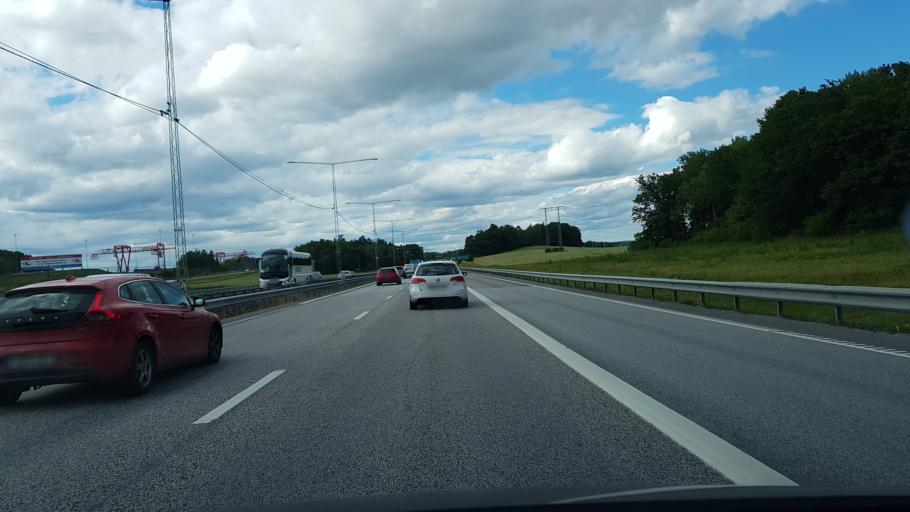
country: SE
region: Stockholm
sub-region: Sigtuna Kommun
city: Rosersberg
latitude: 59.5530
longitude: 17.8990
